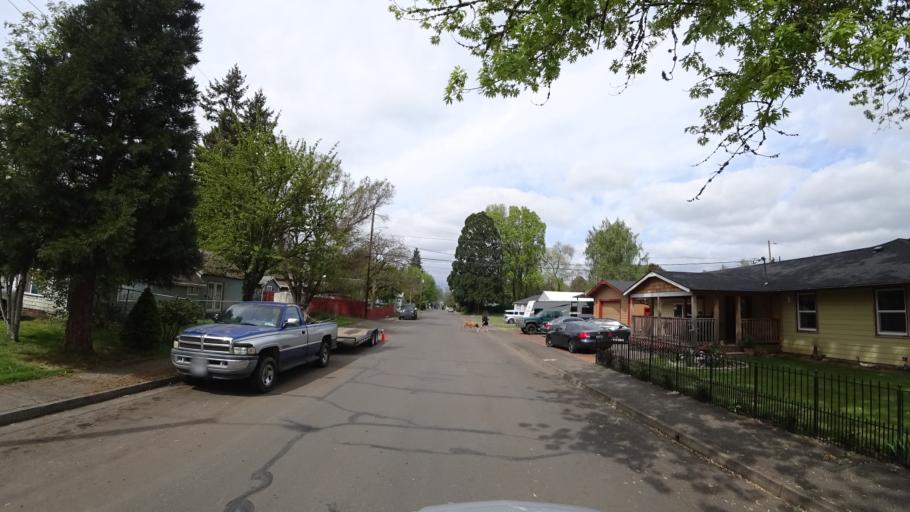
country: US
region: Oregon
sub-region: Washington County
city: Hillsboro
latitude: 45.5240
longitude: -122.9952
